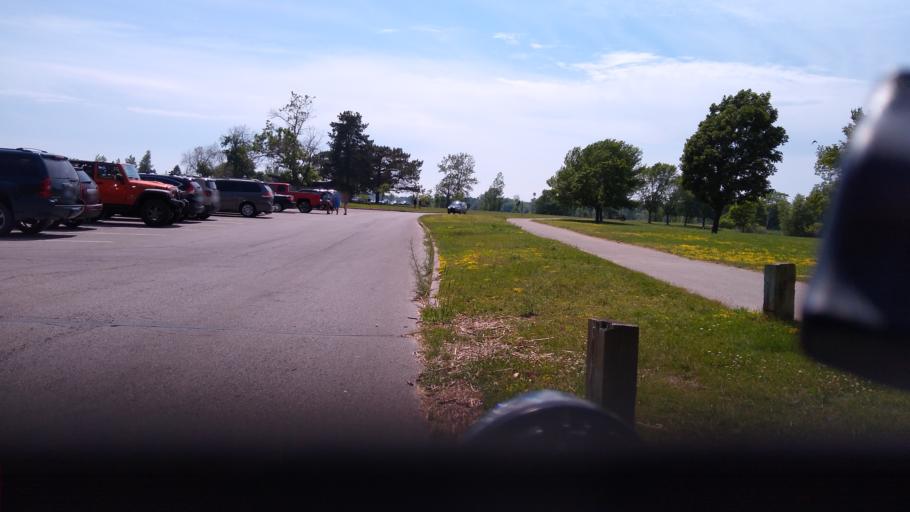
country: US
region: Michigan
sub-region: Delta County
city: Escanaba
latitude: 45.7397
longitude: -87.0454
